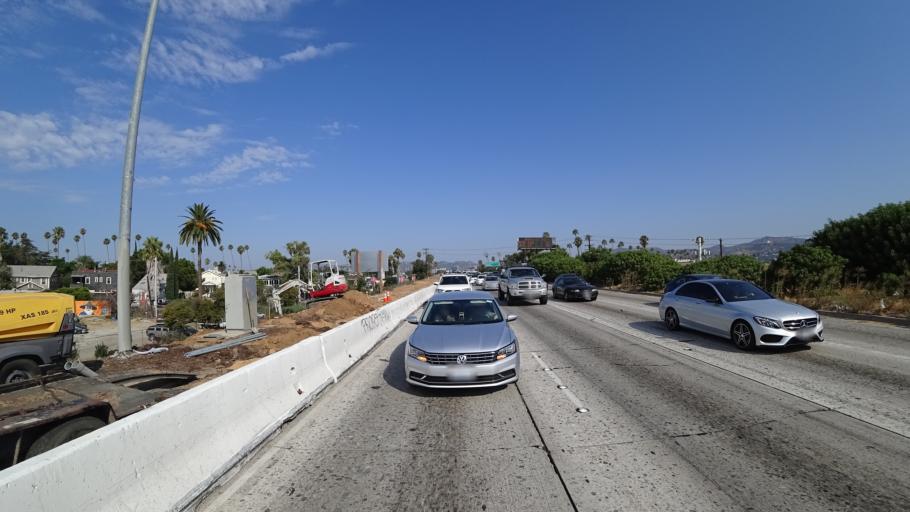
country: US
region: California
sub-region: Los Angeles County
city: Silver Lake
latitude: 34.0828
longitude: -118.2979
